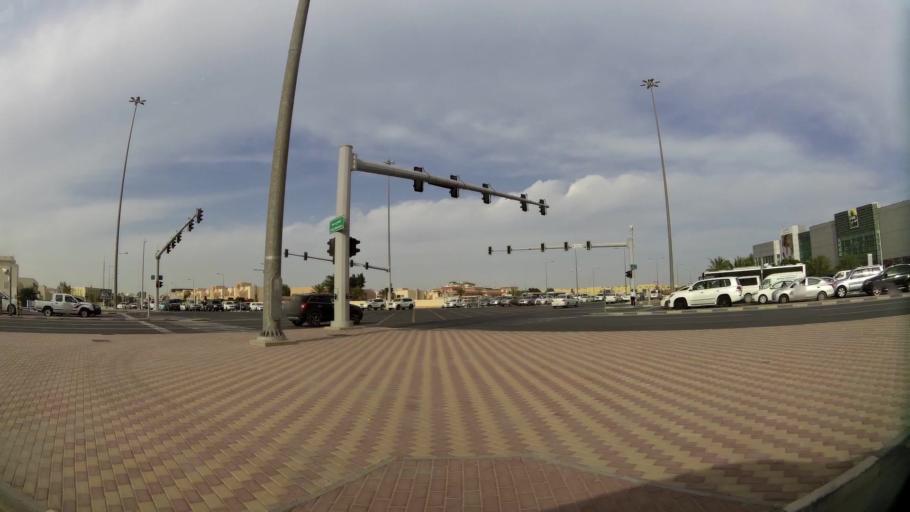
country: QA
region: Baladiyat ad Dawhah
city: Doha
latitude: 25.2539
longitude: 51.5362
